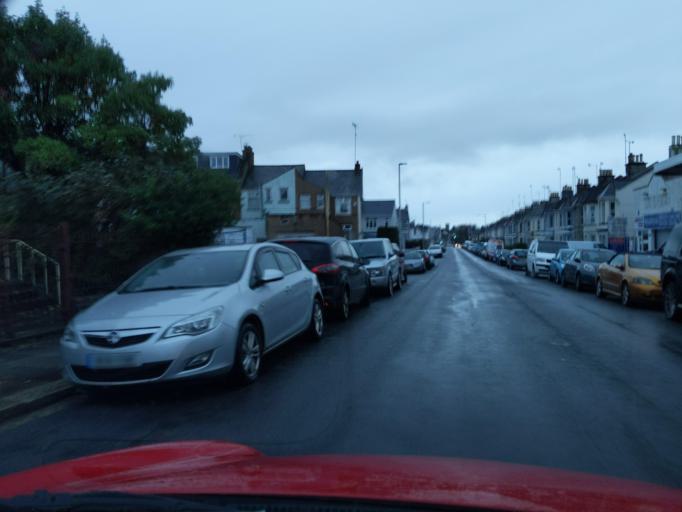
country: GB
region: England
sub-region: Plymouth
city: Plymouth
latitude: 50.3859
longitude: -4.1637
